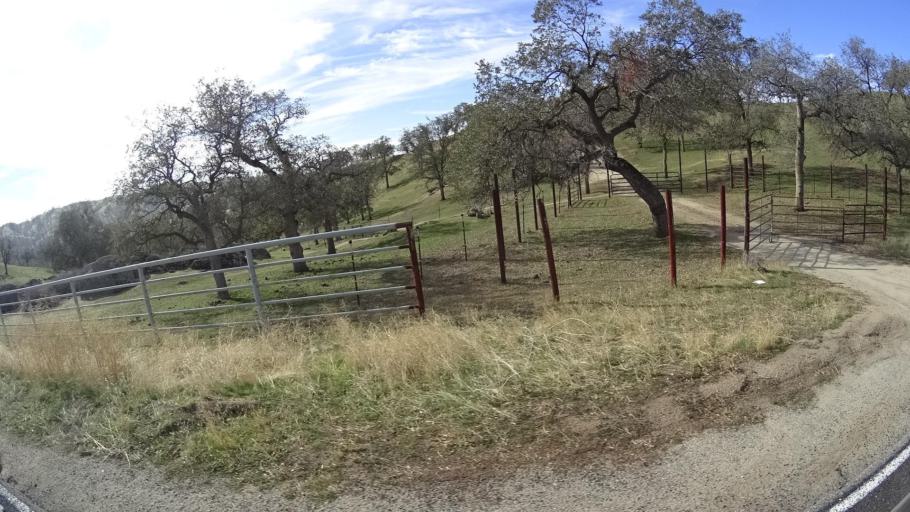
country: US
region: California
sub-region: Kern County
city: Alta Sierra
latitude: 35.6274
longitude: -118.8106
